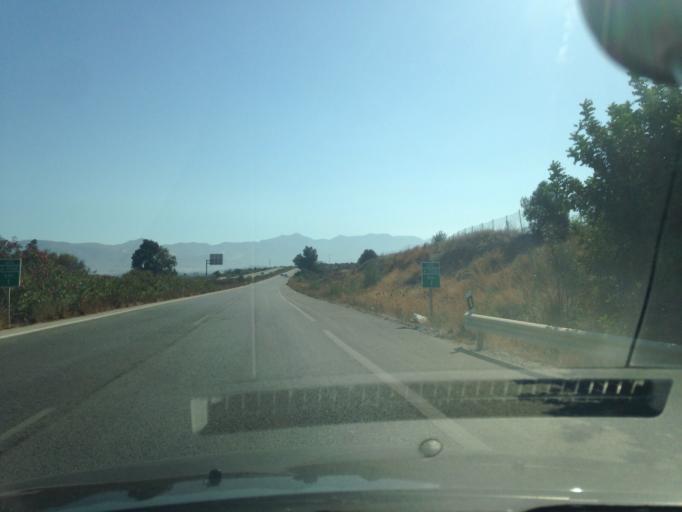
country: ES
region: Andalusia
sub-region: Provincia de Malaga
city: Alhaurin de la Torre
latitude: 36.7276
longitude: -4.5518
